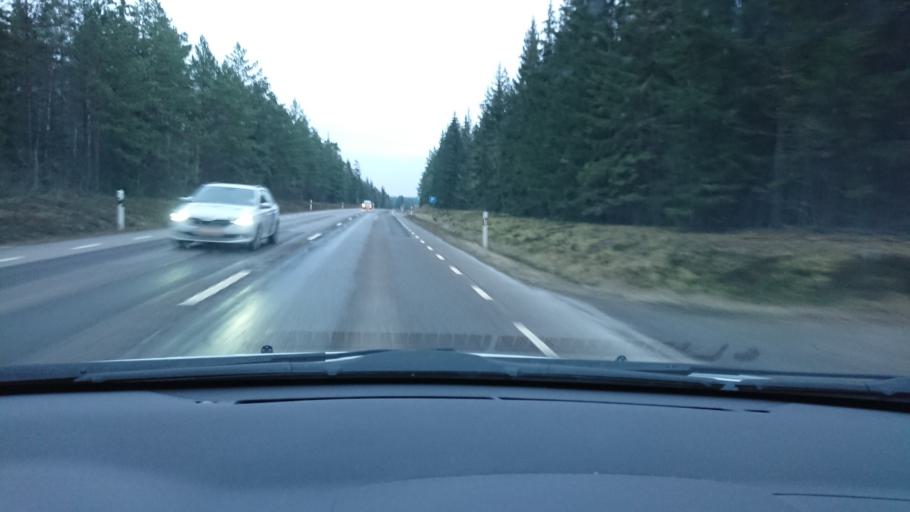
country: SE
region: Kronoberg
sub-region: Vaxjo Kommun
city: Braas
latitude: 57.0546
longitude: 15.1067
